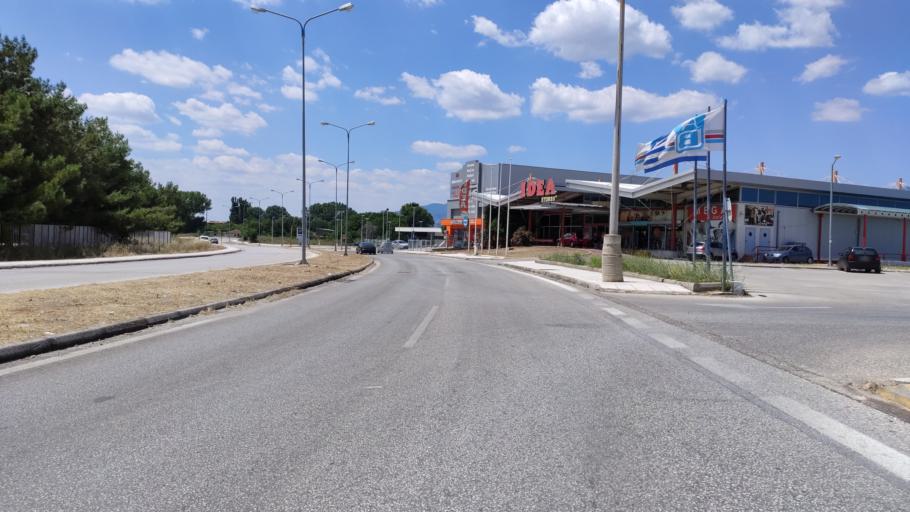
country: GR
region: East Macedonia and Thrace
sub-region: Nomos Rodopis
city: Komotini
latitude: 41.1266
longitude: 25.3910
